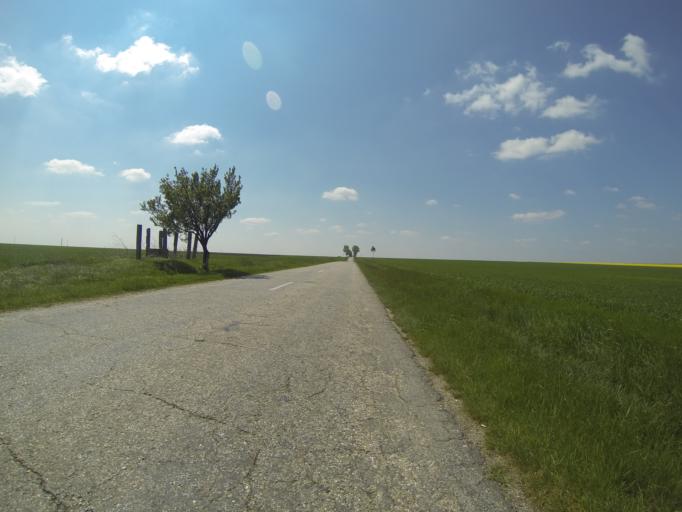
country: RO
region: Dolj
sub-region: Comuna Terpezita
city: Terpezita
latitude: 44.2677
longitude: 23.4747
